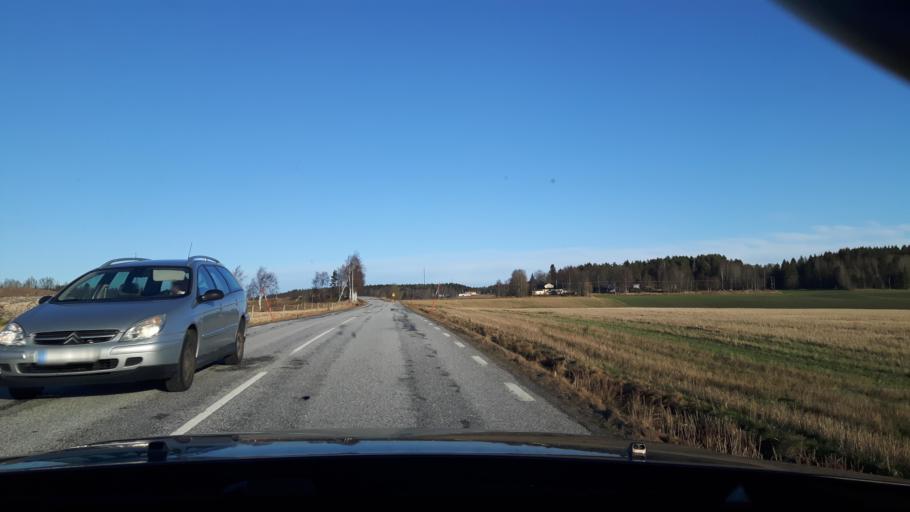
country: SE
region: Vaestra Goetaland
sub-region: Munkedals Kommun
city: Munkedal
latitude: 58.6326
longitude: 11.7750
